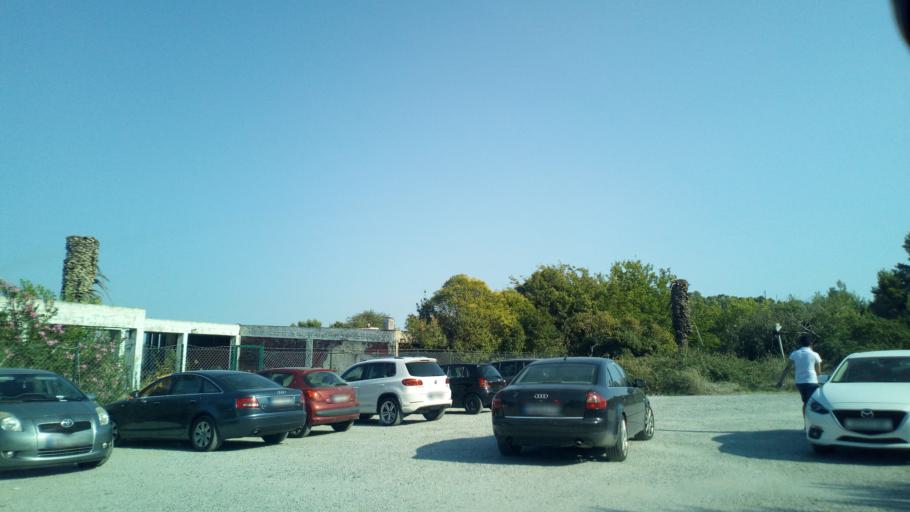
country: GR
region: Central Macedonia
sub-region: Nomos Chalkidikis
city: Pefkochori
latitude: 39.9593
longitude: 23.6761
